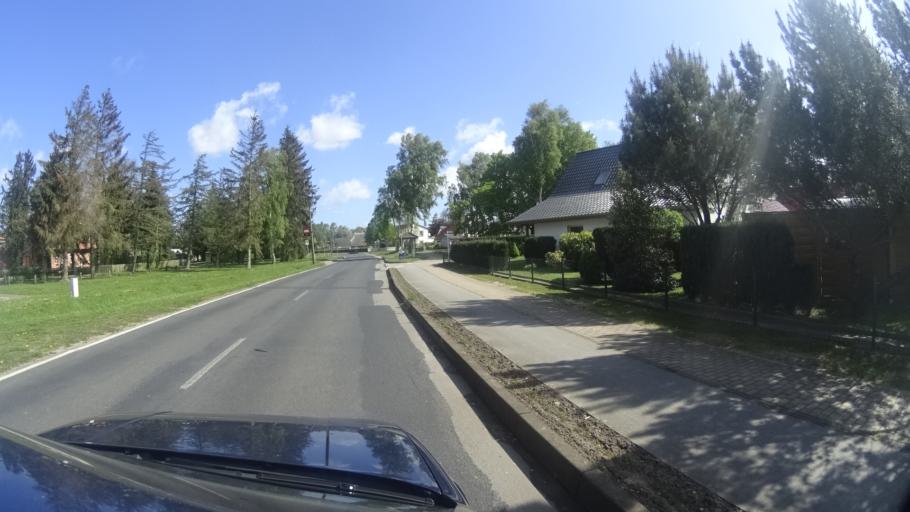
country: DE
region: Mecklenburg-Vorpommern
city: Born
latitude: 54.3597
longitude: 12.6010
